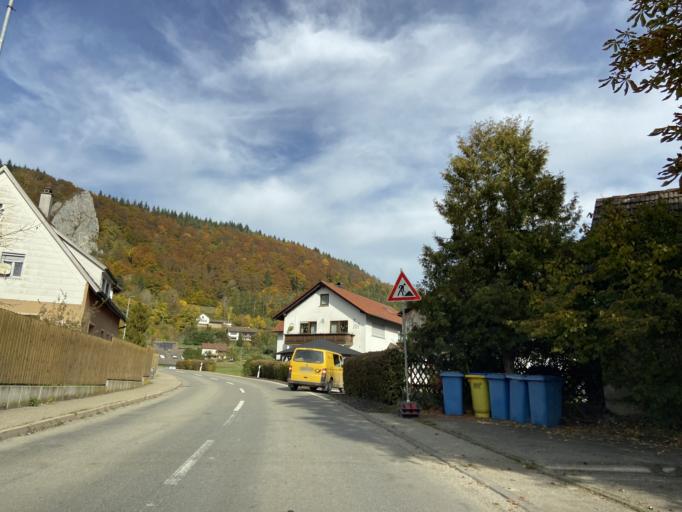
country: DE
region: Baden-Wuerttemberg
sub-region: Tuebingen Region
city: Schwenningen
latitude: 48.0852
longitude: 9.0395
